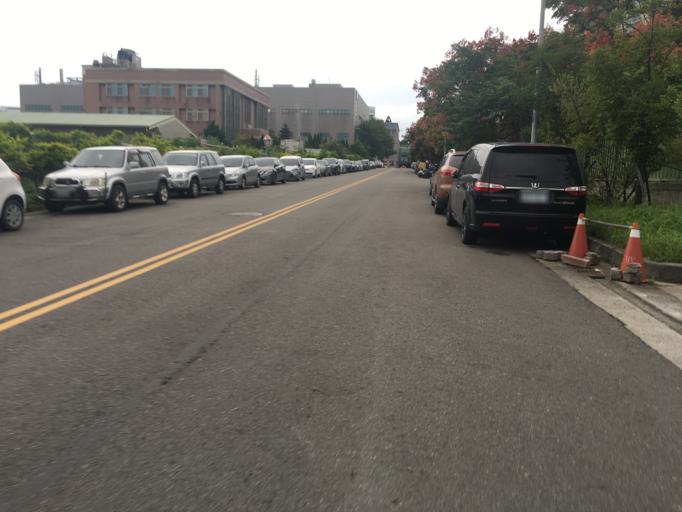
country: TW
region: Taiwan
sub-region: Hsinchu
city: Hsinchu
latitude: 24.7250
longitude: 120.9100
